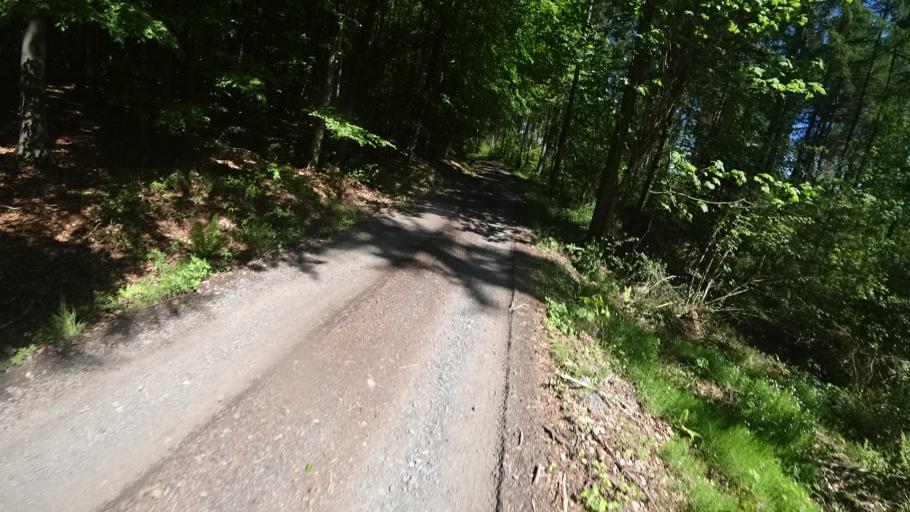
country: DE
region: Rheinland-Pfalz
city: Elkenroth
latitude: 50.7455
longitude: 7.8866
